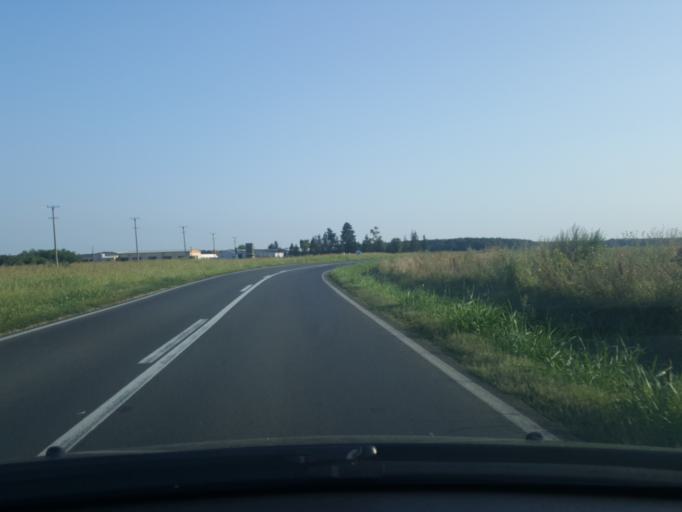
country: RS
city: Hrtkovci
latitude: 44.8522
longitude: 19.7709
